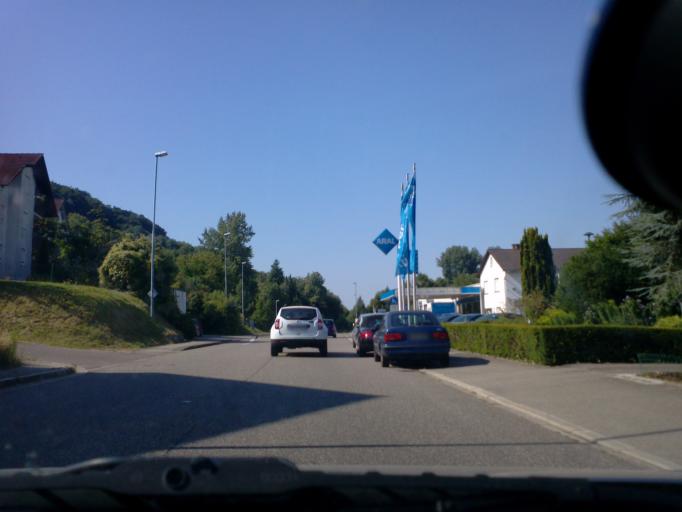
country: DE
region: Baden-Wuerttemberg
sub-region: Karlsruhe Region
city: Weingarten
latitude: 49.0808
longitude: 8.5500
